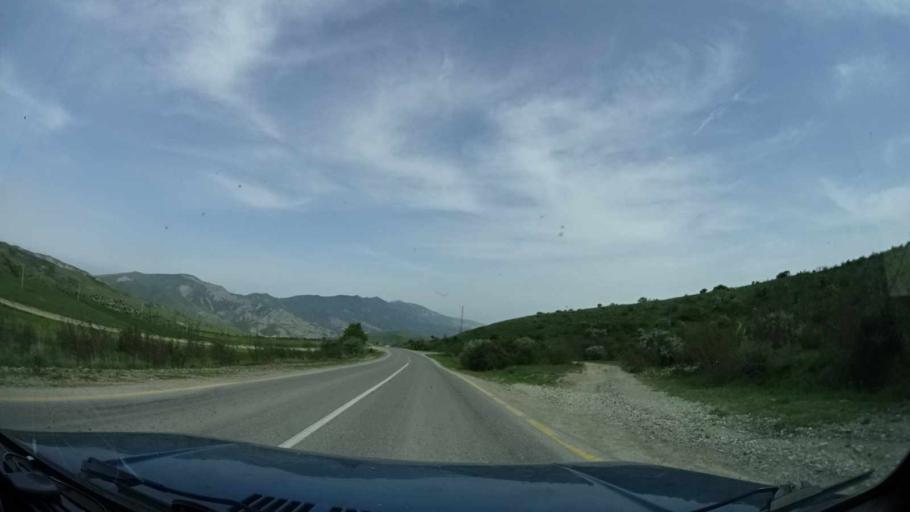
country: AZ
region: Xizi
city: Khyzy
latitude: 40.9058
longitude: 49.1039
